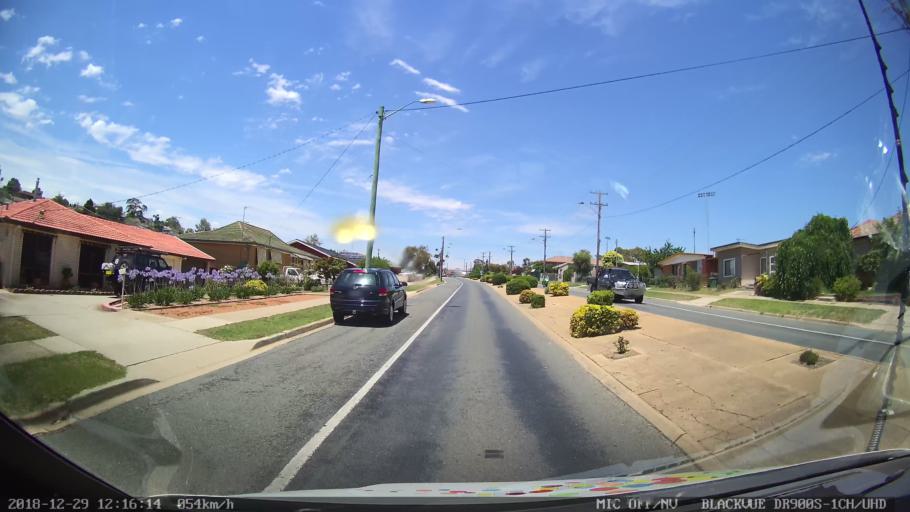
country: AU
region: New South Wales
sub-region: Queanbeyan
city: Queanbeyan
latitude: -35.3679
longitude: 149.2332
